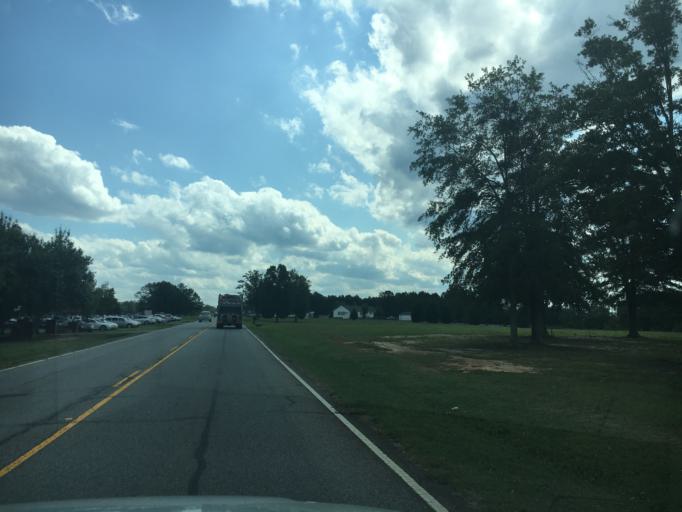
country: US
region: South Carolina
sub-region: Anderson County
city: Williamston
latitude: 34.5955
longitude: -82.4987
